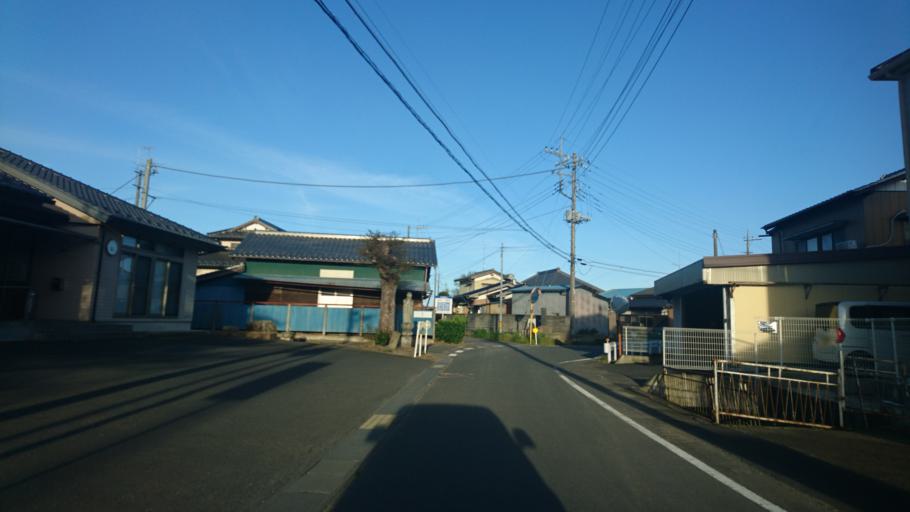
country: JP
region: Ibaraki
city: Ishige
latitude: 36.1713
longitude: 139.9956
